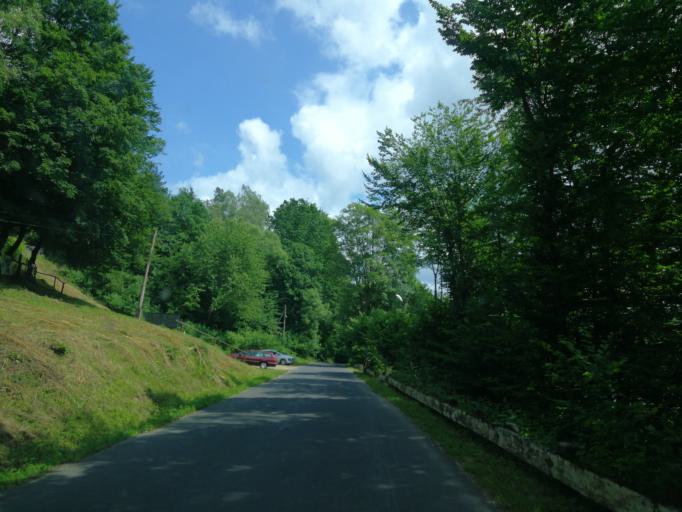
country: PL
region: Subcarpathian Voivodeship
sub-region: Powiat leski
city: Uherce Mineralne
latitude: 49.4295
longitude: 22.4148
